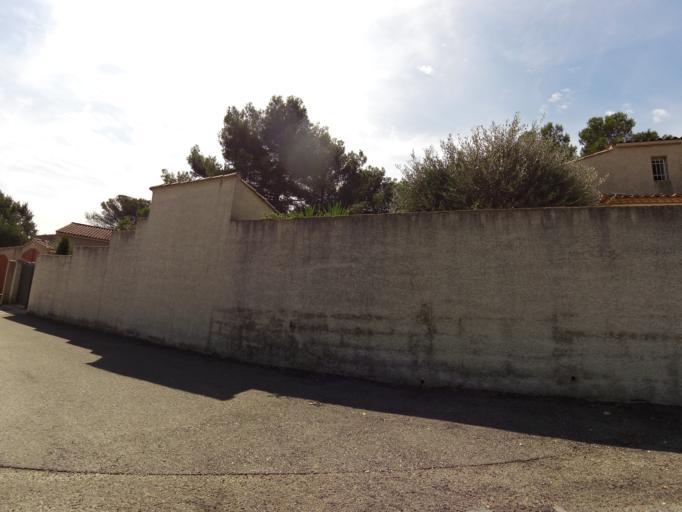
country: FR
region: Languedoc-Roussillon
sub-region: Departement du Gard
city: Mus
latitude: 43.7418
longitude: 4.2061
